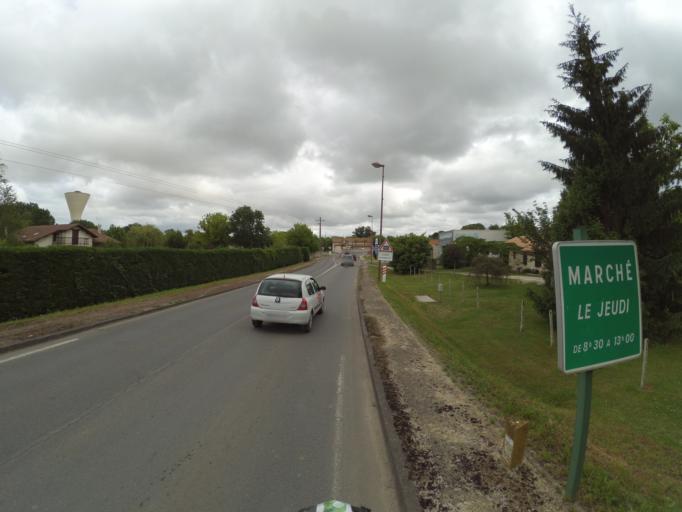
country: FR
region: Aquitaine
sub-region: Departement de la Gironde
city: Cantenac
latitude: 45.0236
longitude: -0.6394
